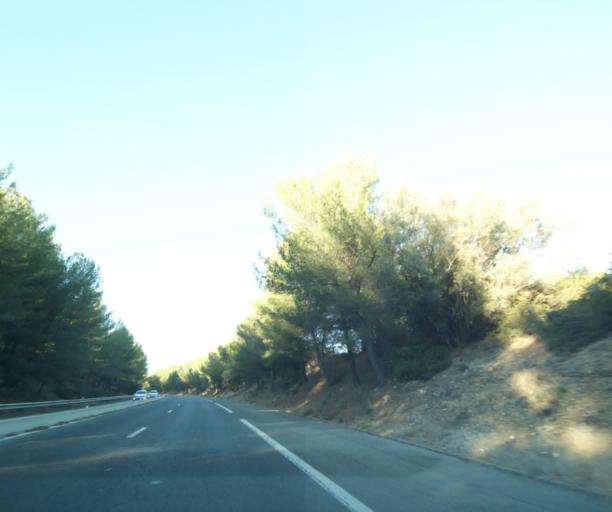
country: FR
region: Provence-Alpes-Cote d'Azur
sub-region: Departement du Var
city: Saint-Cyr-sur-Mer
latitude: 43.1877
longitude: 5.6915
